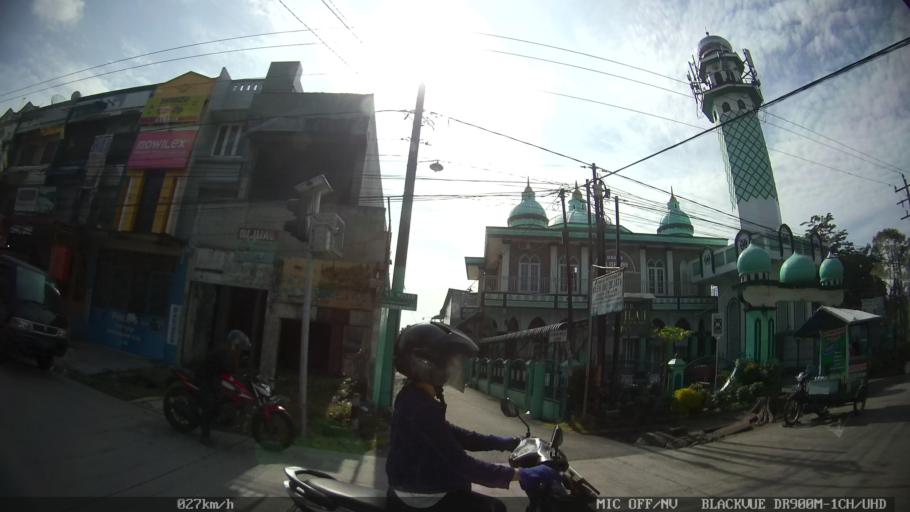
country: ID
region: North Sumatra
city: Medan
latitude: 3.5948
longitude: 98.6446
